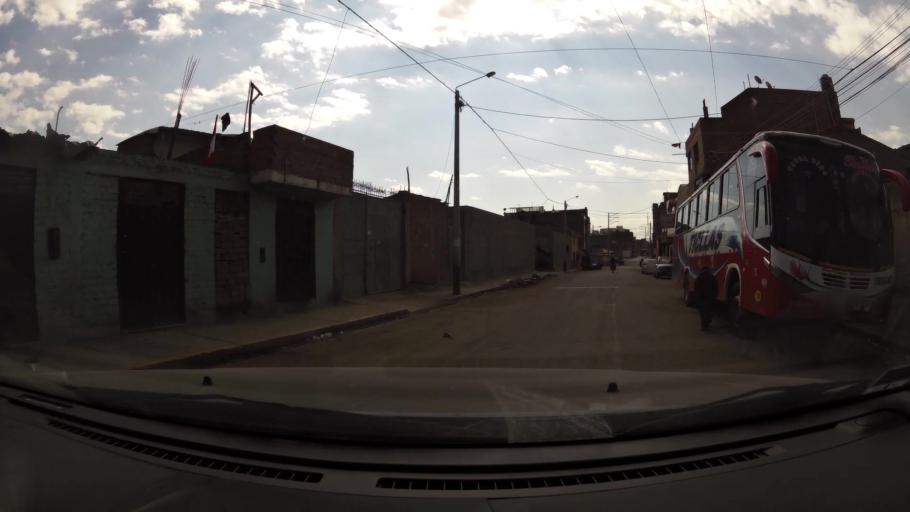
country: PE
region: Junin
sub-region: Provincia de Huancayo
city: Huancayo
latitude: -12.0776
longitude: -75.2036
